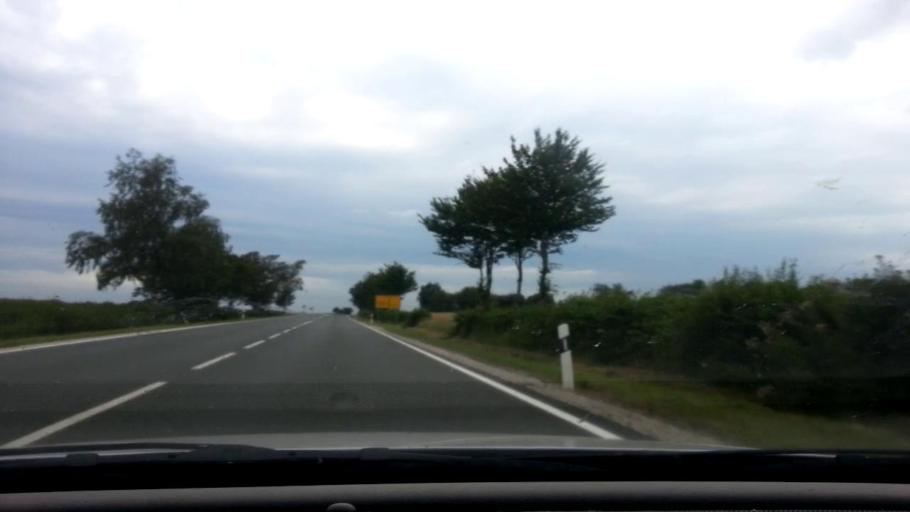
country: DE
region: Bavaria
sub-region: Upper Palatinate
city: Erbendorf
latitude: 49.8516
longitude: 11.9812
